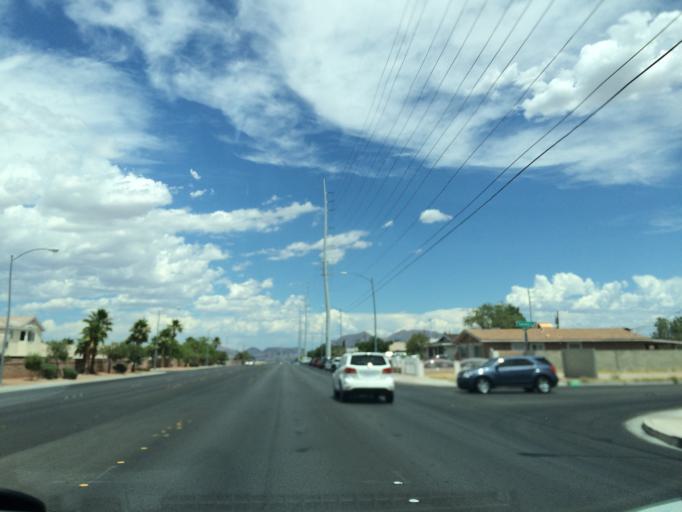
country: US
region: Nevada
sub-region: Clark County
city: Las Vegas
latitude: 36.2031
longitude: -115.1566
